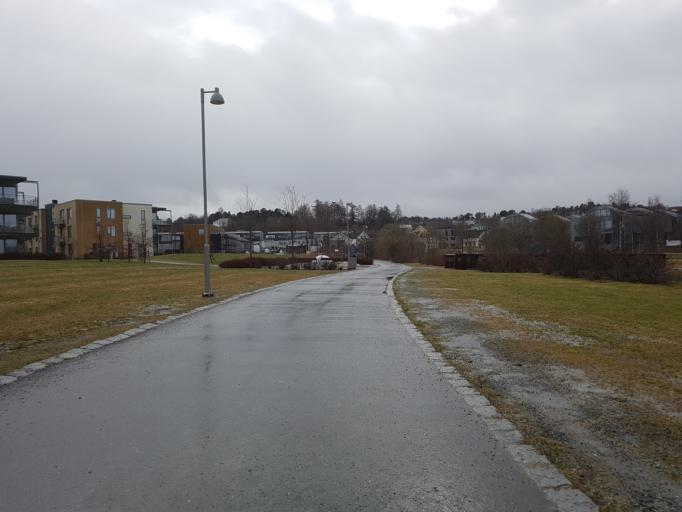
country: NO
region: Sor-Trondelag
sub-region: Trondheim
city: Trondheim
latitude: 63.4360
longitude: 10.5004
